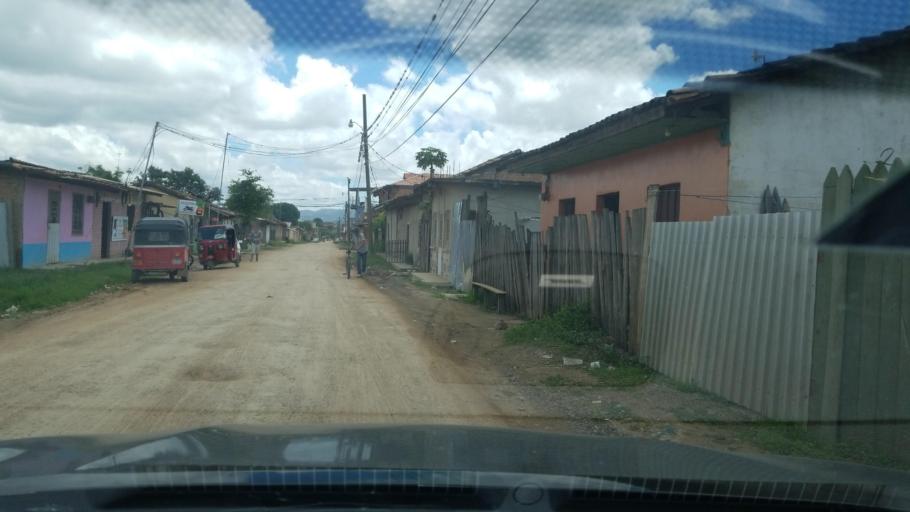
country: HN
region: Francisco Morazan
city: Talanga
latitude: 14.3994
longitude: -87.0798
